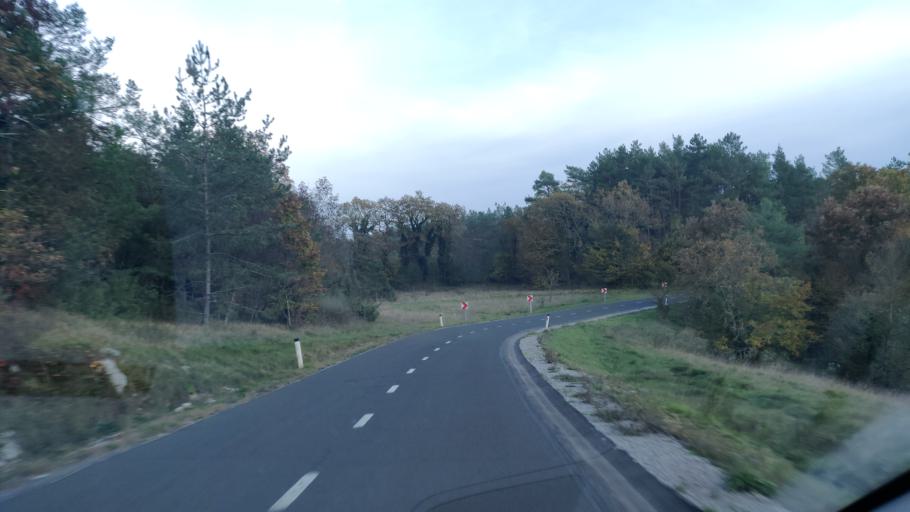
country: SI
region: Sezana
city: Sezana
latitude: 45.7712
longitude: 13.8787
